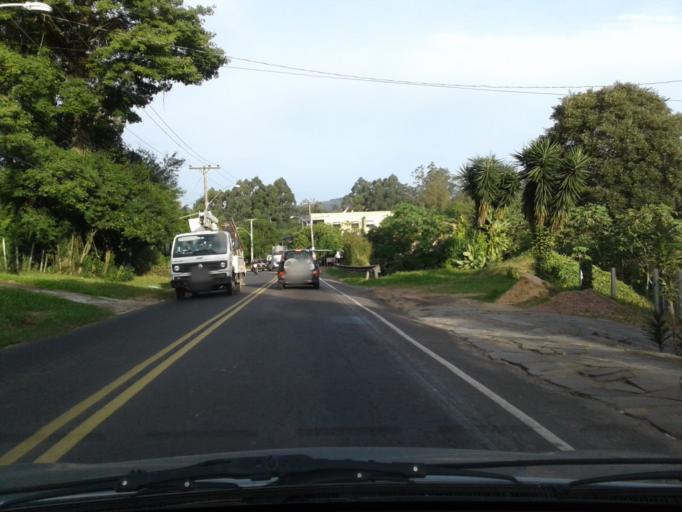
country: BR
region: Rio Grande do Sul
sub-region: Porto Alegre
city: Porto Alegre
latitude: -30.1119
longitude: -51.2177
